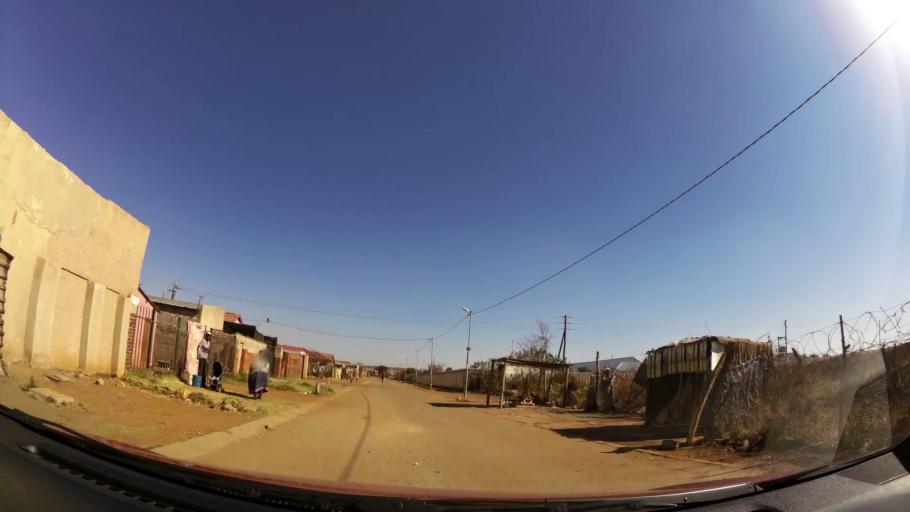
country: ZA
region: Gauteng
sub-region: City of Johannesburg Metropolitan Municipality
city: Soweto
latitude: -26.2172
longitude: 27.8288
